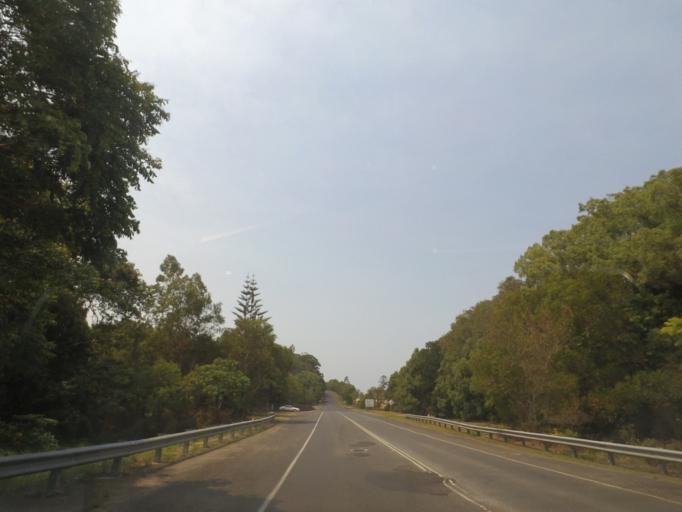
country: AU
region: New South Wales
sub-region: Byron Shire
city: Brunswick Heads
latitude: -28.5139
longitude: 153.5298
